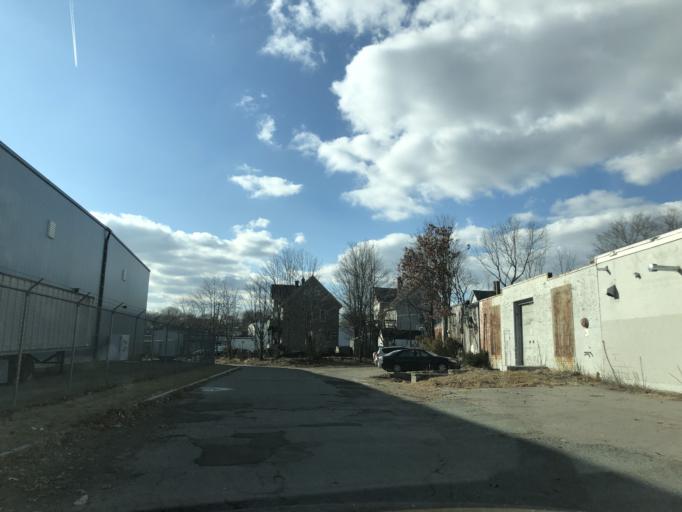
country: US
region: Massachusetts
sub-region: Plymouth County
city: Brockton
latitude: 42.1084
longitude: -71.0205
